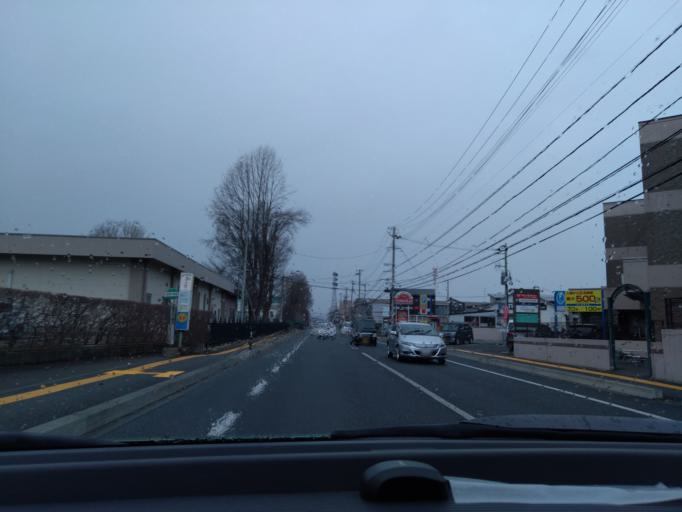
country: JP
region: Iwate
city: Morioka-shi
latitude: 39.7158
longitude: 141.1393
